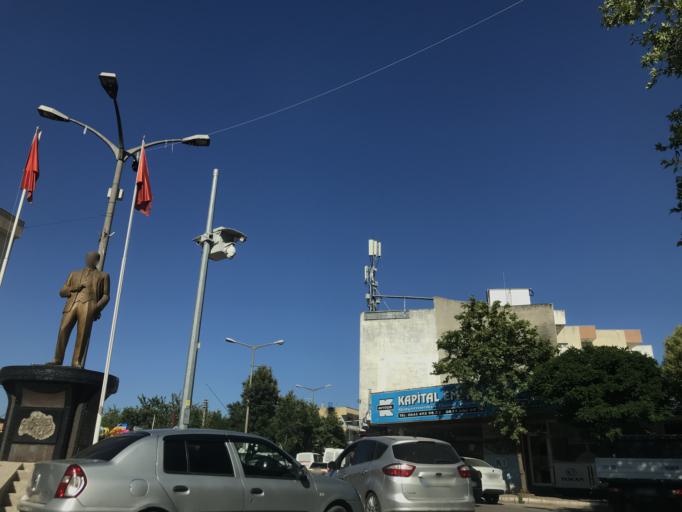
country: TR
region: Aydin
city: Davutlar
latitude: 37.7337
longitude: 27.2956
